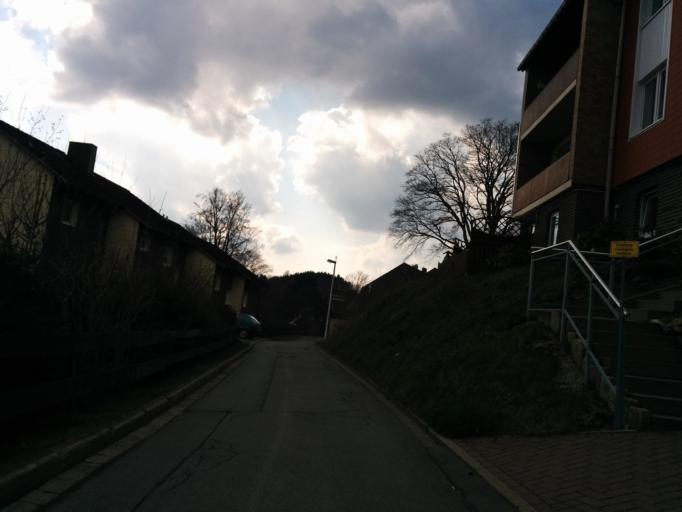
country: DE
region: Lower Saxony
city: Sankt Andreasberg
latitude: 51.7097
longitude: 10.5212
